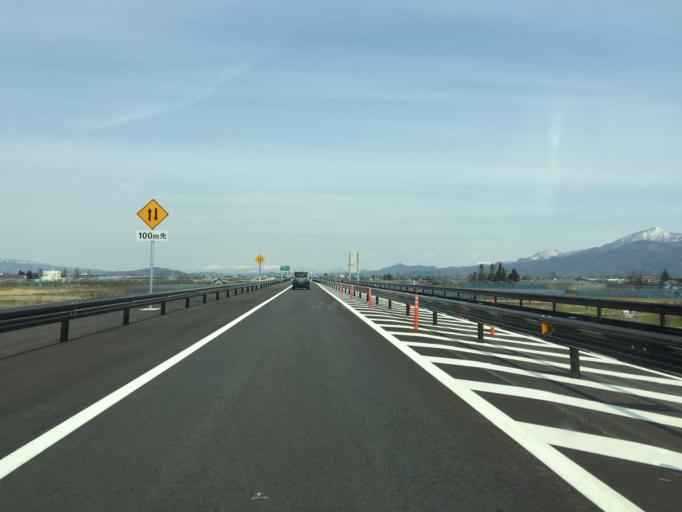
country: JP
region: Yamagata
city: Higashine
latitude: 38.4173
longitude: 140.3498
